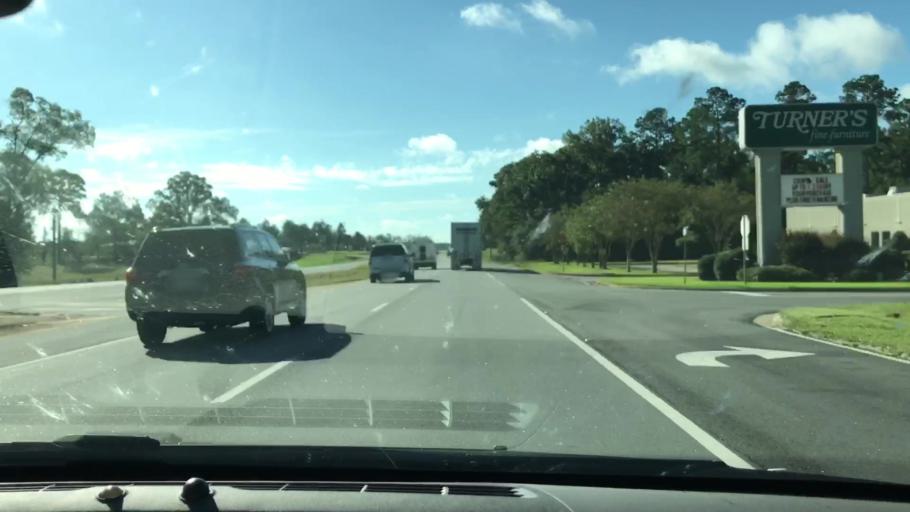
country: US
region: Georgia
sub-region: Dougherty County
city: Albany
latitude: 31.6401
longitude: -84.2516
